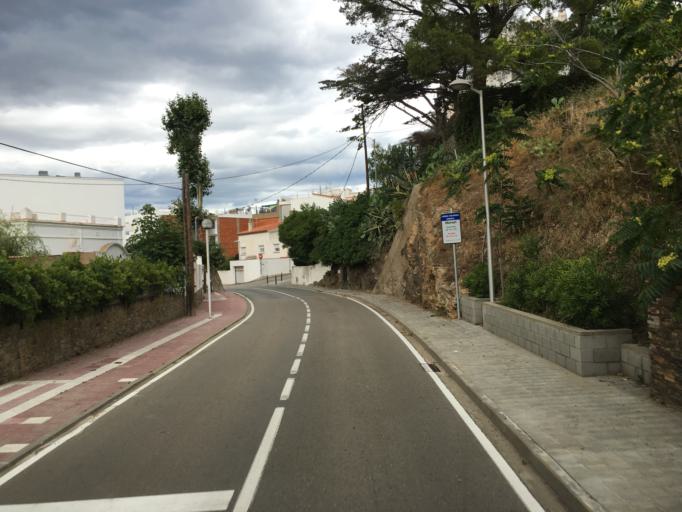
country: ES
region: Catalonia
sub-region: Provincia de Girona
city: Llanca
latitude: 42.3347
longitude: 3.2040
